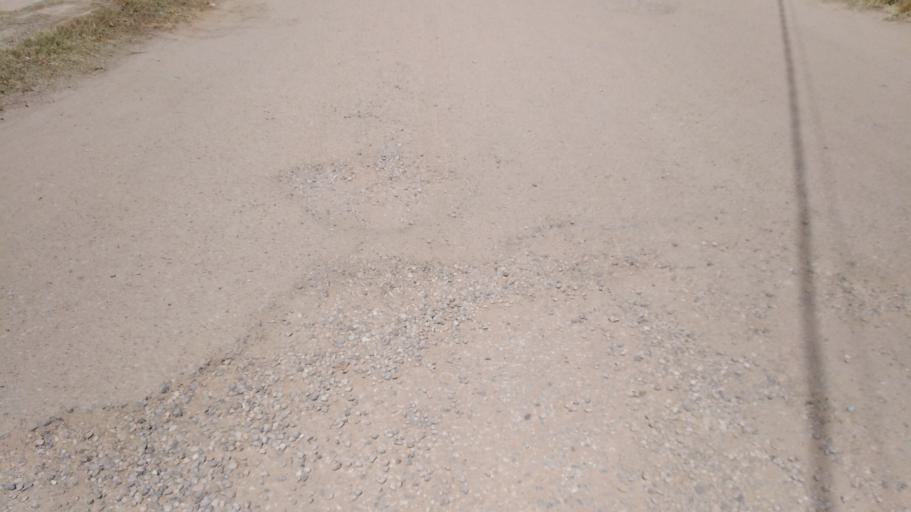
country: TN
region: Qabis
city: Matmata
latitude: 33.6133
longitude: 10.2869
